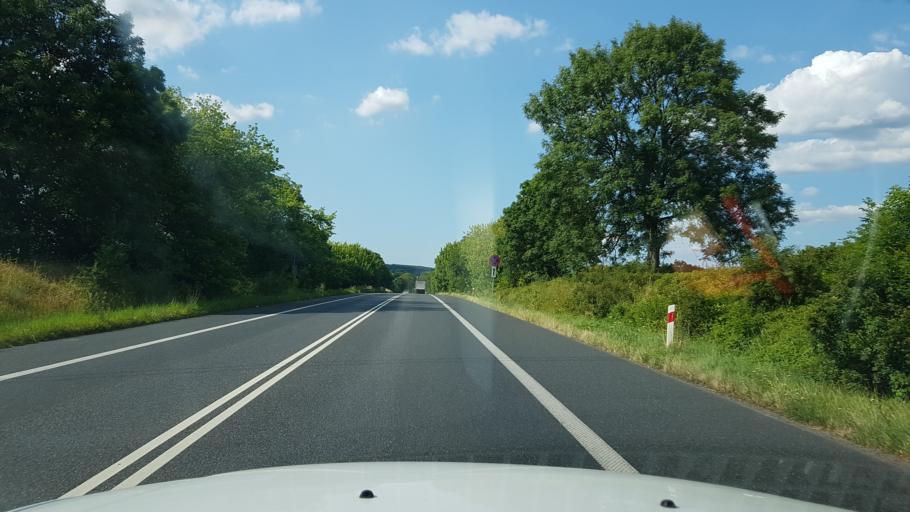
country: PL
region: West Pomeranian Voivodeship
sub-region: Powiat gryfinski
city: Stare Czarnowo
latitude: 53.2655
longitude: 14.7837
